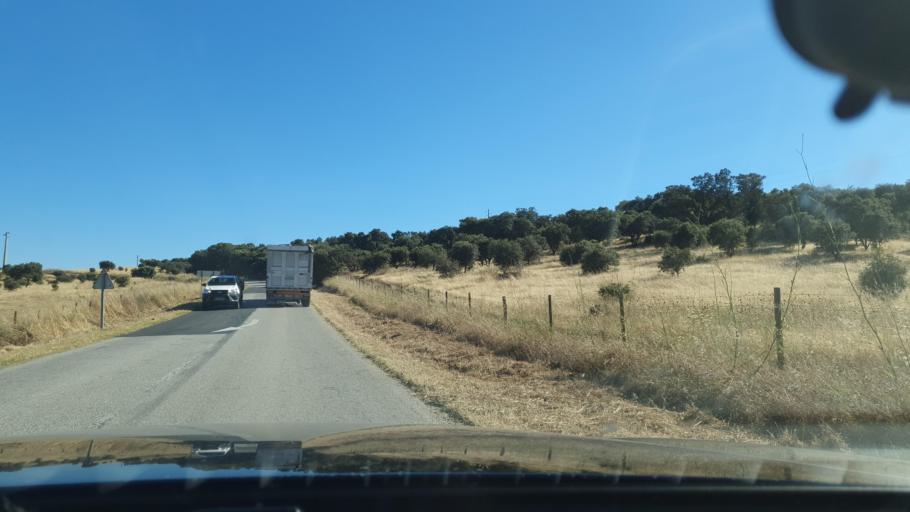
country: PT
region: Evora
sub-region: Alandroal
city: Alandroal
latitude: 38.7315
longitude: -7.4049
